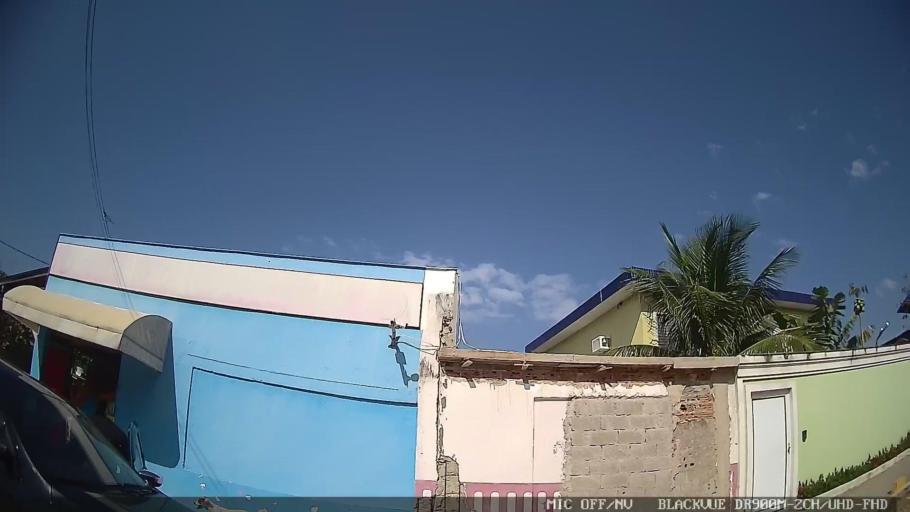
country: BR
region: Sao Paulo
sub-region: Guaruja
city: Guaruja
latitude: -23.9778
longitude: -46.1950
